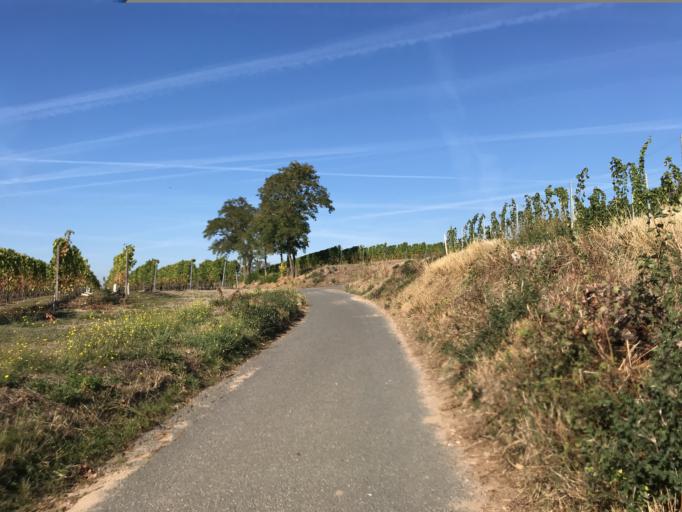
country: DE
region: Hesse
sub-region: Regierungsbezirk Darmstadt
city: Hochheim am Main
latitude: 50.0159
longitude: 8.3116
